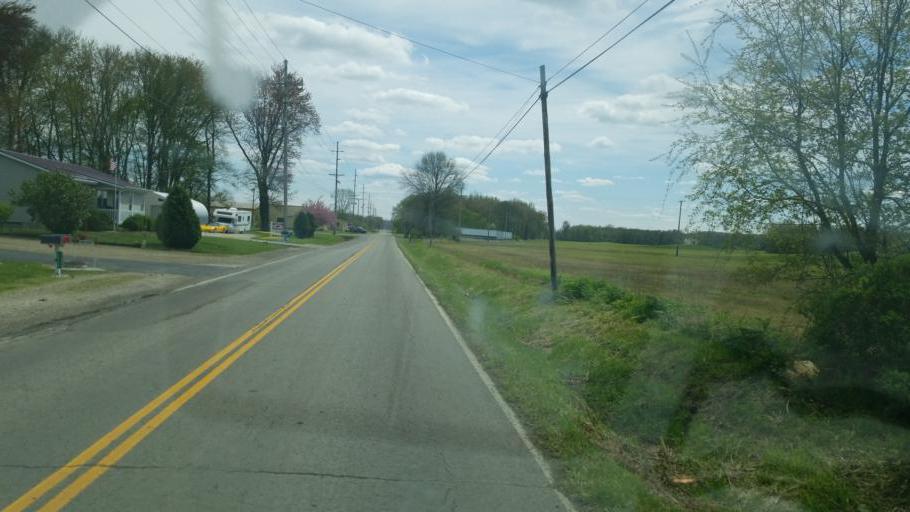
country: US
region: Ohio
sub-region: Wayne County
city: Wooster
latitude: 40.7840
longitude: -81.9442
